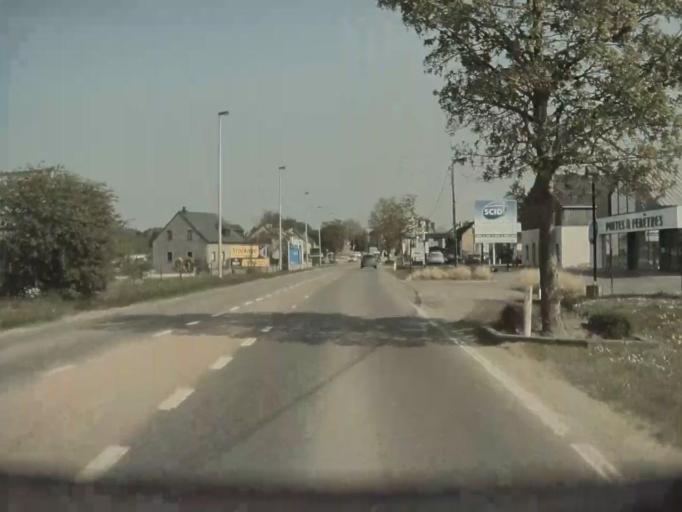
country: BE
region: Wallonia
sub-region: Province de Namur
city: Dinant
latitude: 50.2607
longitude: 4.9699
